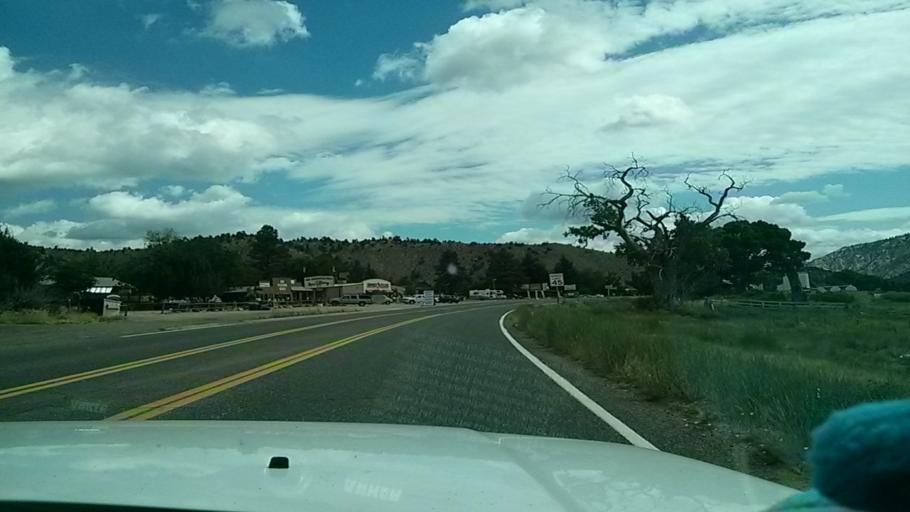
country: US
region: Utah
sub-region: Kane County
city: Kanab
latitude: 37.2692
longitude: -112.6509
